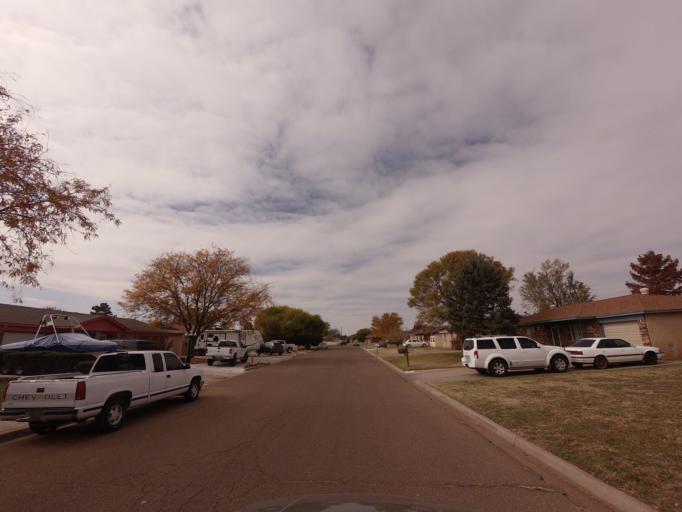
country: US
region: New Mexico
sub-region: Curry County
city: Clovis
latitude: 34.4299
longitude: -103.2236
